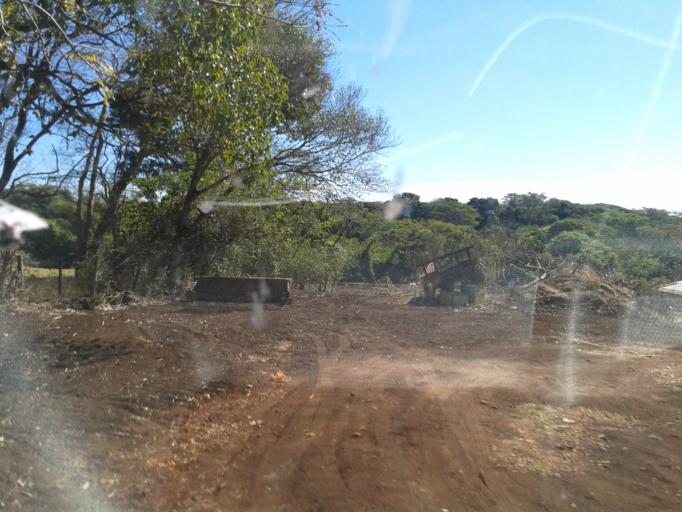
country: BR
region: Minas Gerais
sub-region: Capinopolis
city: Capinopolis
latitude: -18.6868
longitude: -49.5869
